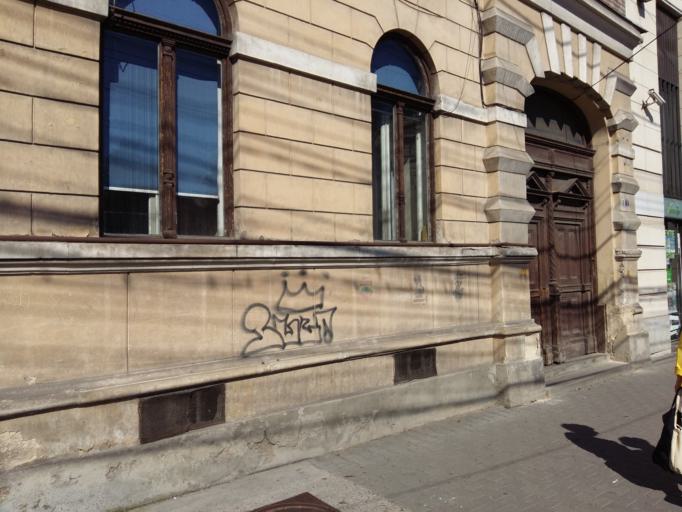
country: RO
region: Cluj
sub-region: Municipiul Cluj-Napoca
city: Cluj-Napoca
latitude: 46.7711
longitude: 23.5962
